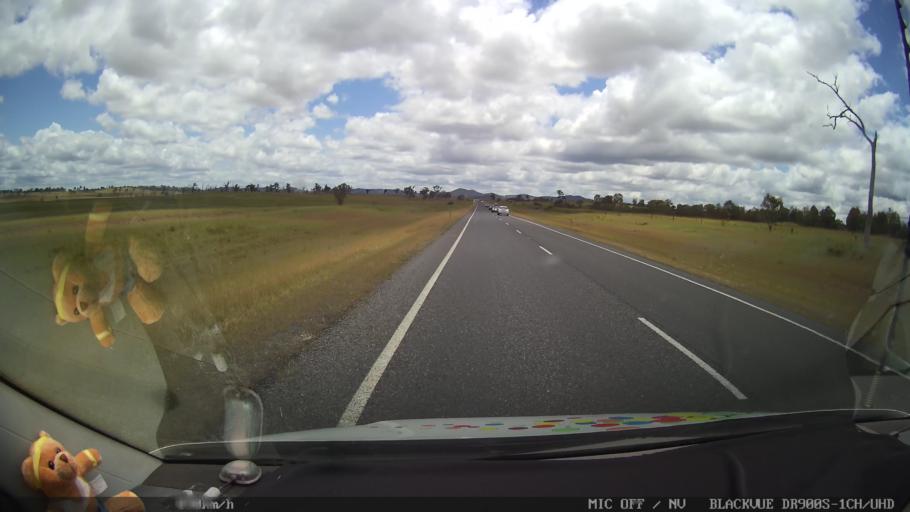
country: AU
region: New South Wales
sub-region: Glen Innes Severn
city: Glen Innes
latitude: -29.4107
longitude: 151.8676
